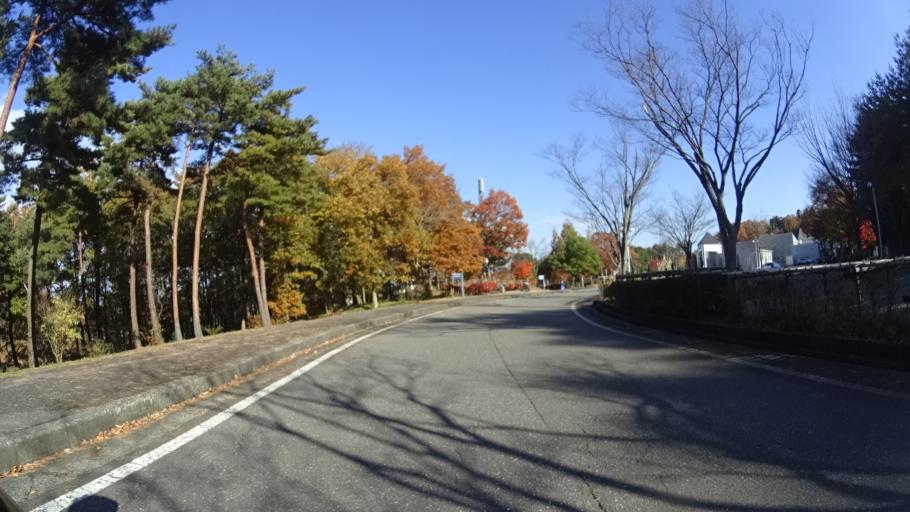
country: JP
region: Niigata
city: Itoigawa
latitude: 37.0247
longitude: 137.8688
